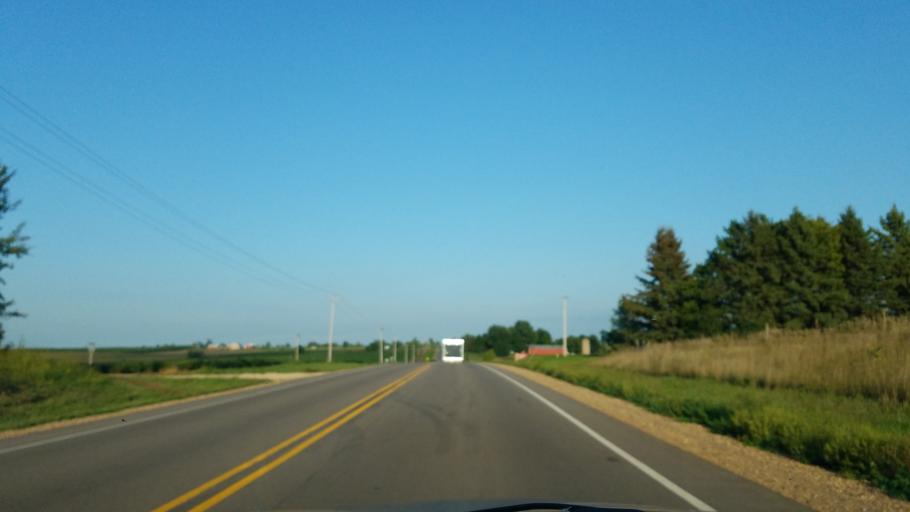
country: US
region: Wisconsin
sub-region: Saint Croix County
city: New Richmond
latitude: 45.0789
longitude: -92.4993
